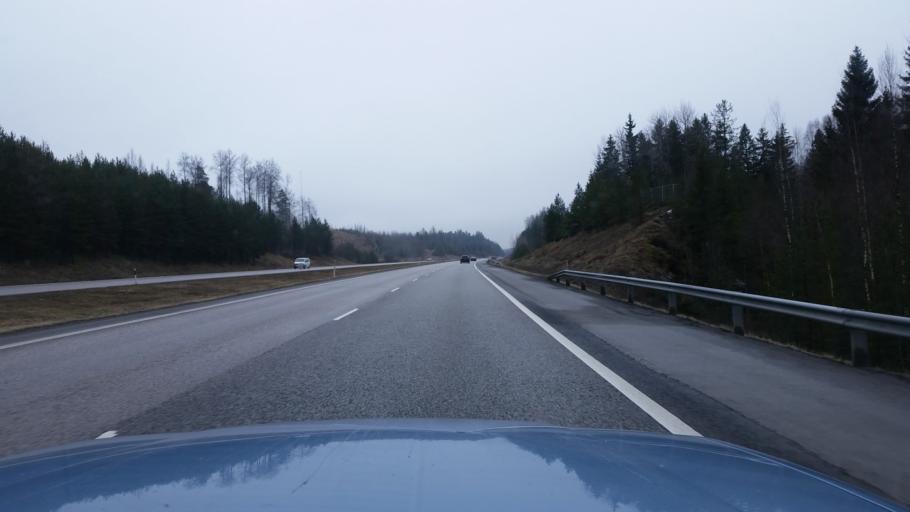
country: FI
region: Uusimaa
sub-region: Helsinki
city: Nurmijaervi
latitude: 60.3791
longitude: 24.8143
